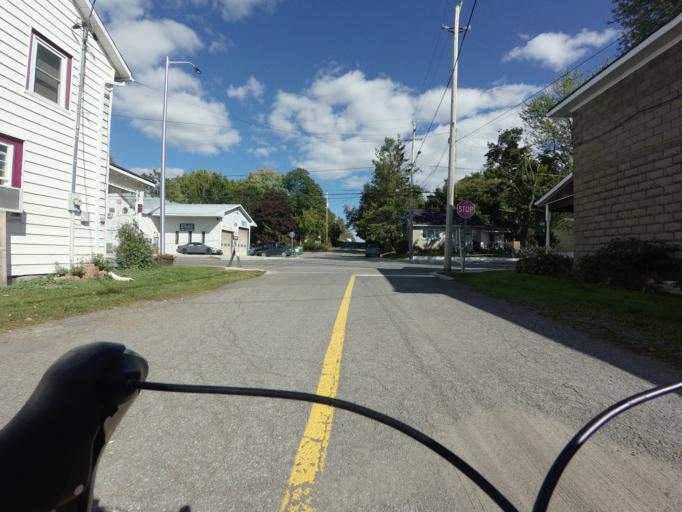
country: CA
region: Ontario
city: Bells Corners
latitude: 45.1503
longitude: -75.6477
